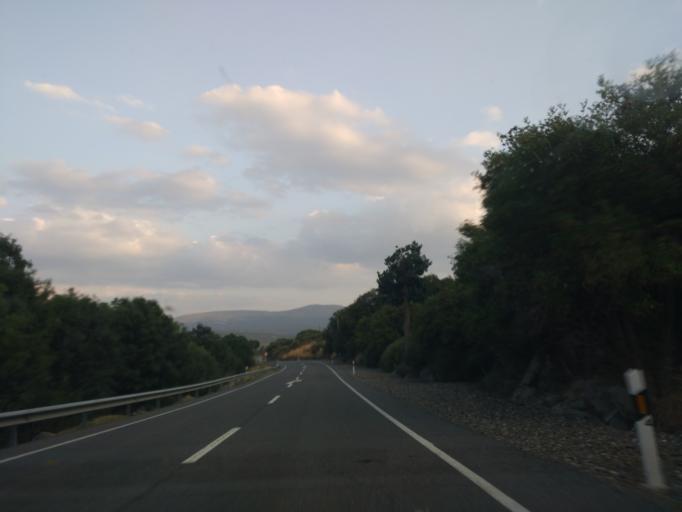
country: ES
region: Castille and Leon
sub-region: Provincia de Avila
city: Hoyos de Miguel Munoz
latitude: 40.4030
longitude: -5.0294
